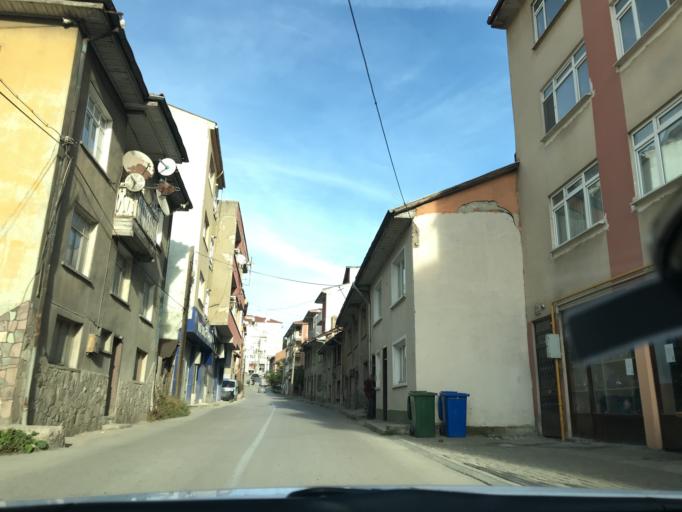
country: TR
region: Bolu
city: Bolu
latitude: 40.7328
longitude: 31.6119
